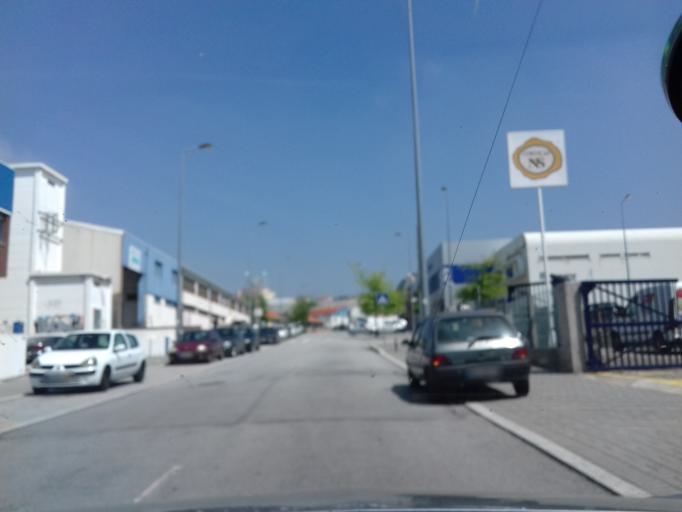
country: PT
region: Porto
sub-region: Vila Nova de Gaia
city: Canelas
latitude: 41.0928
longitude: -8.6030
